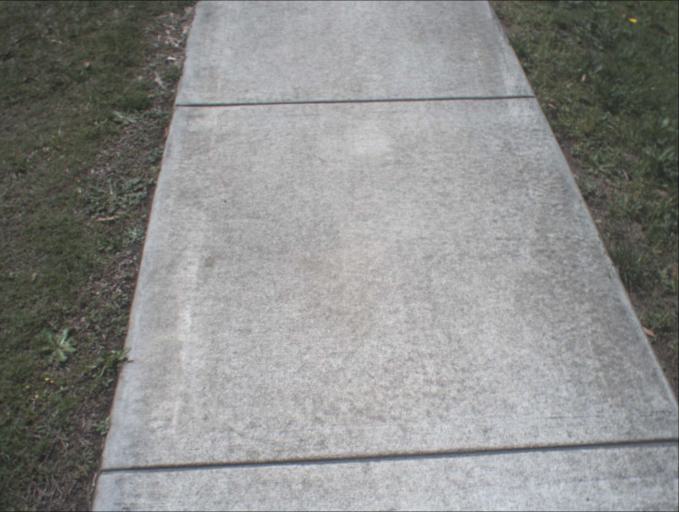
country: AU
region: Queensland
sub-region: Logan
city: Park Ridge South
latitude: -27.7282
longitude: 153.0444
